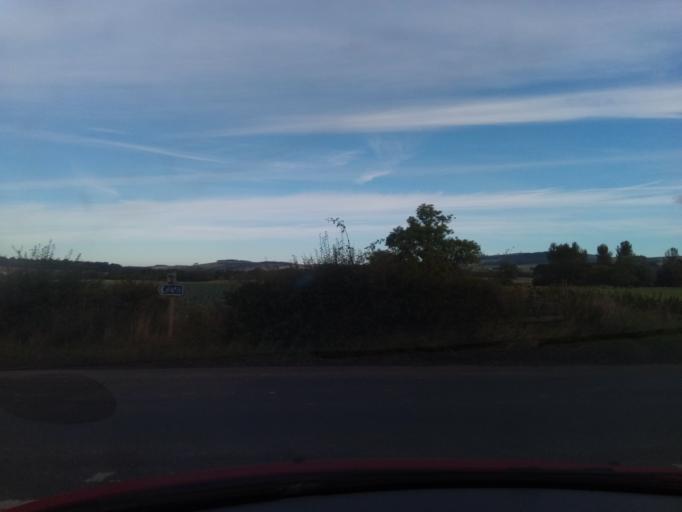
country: GB
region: Scotland
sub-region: The Scottish Borders
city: Kelso
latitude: 55.5174
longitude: -2.3877
